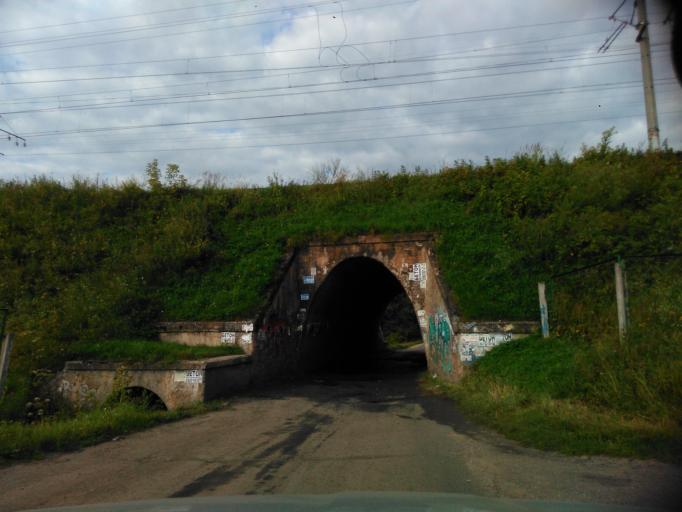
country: RU
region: Moskovskaya
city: Peshki
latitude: 56.1268
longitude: 37.0251
